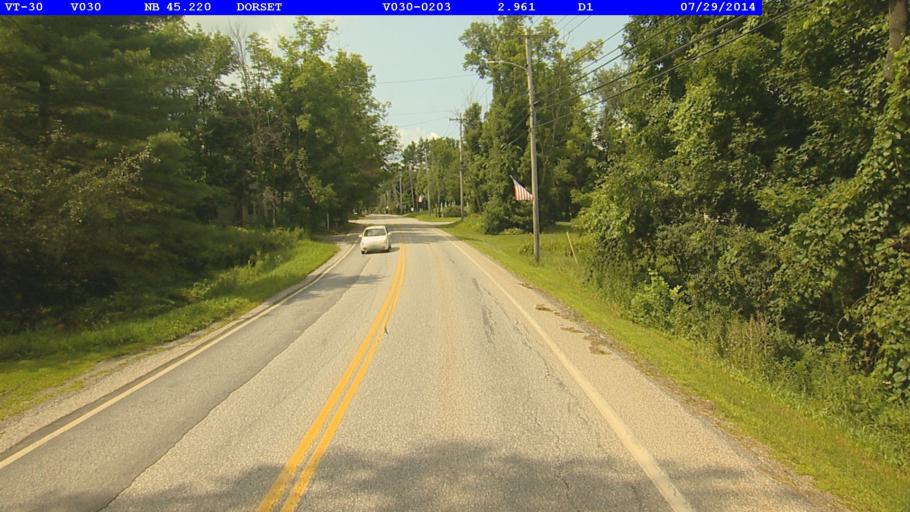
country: US
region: Vermont
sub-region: Bennington County
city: Manchester Center
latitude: 43.2503
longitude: -73.0937
